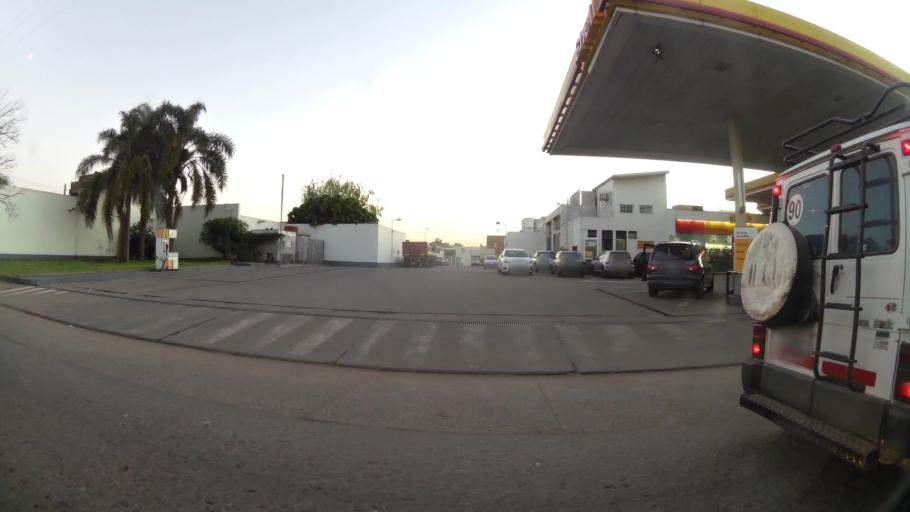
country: AR
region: Santa Fe
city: Santa Fe de la Vera Cruz
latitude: -31.6017
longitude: -60.7121
